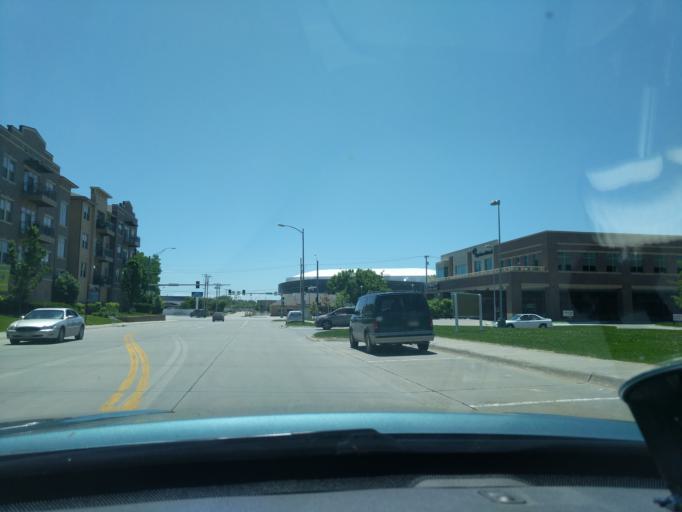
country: US
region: Nebraska
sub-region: Douglas County
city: Ralston
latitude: 41.2389
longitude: -96.0120
